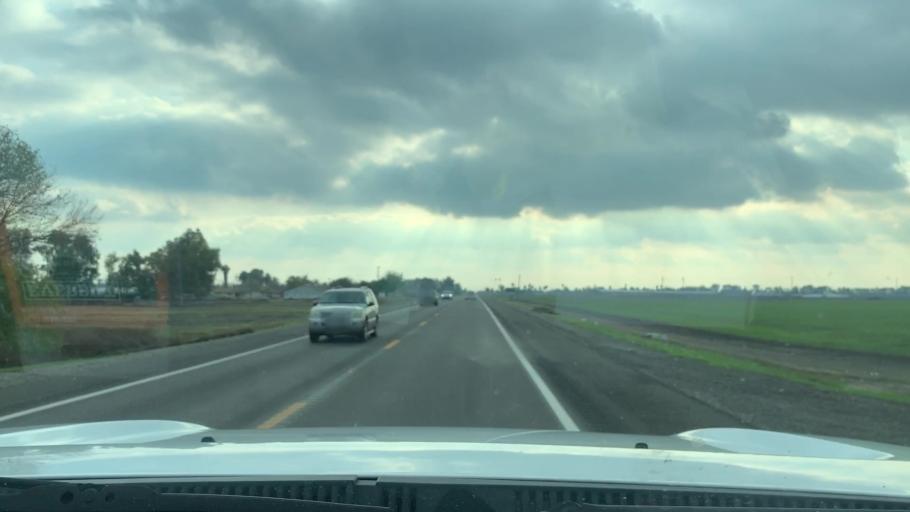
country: US
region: California
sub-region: Kings County
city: Stratford
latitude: 36.1991
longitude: -119.8210
